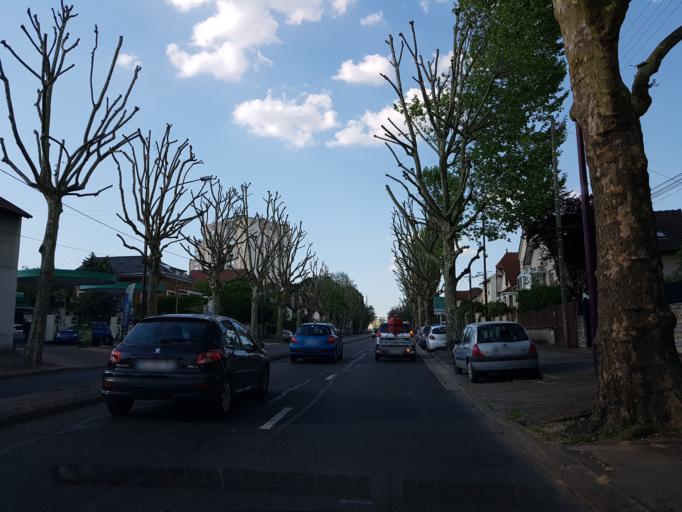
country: FR
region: Ile-de-France
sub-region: Departement du Val-de-Marne
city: L'Hay-les-Roses
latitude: 48.7770
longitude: 2.3403
